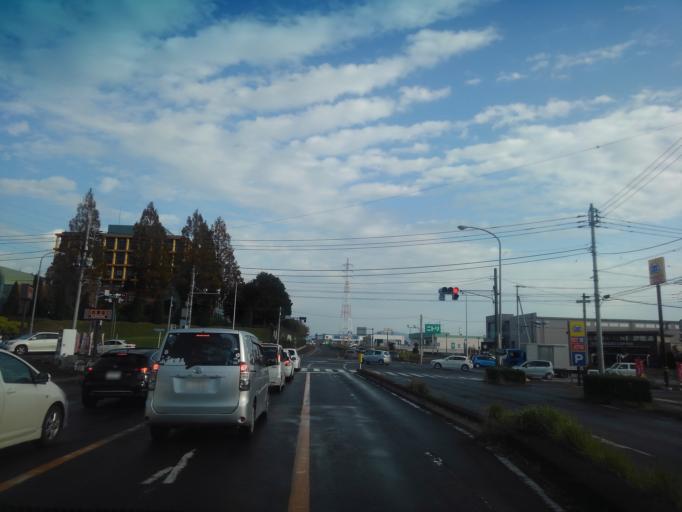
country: JP
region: Ibaraki
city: Naka
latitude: 36.0720
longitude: 140.0844
